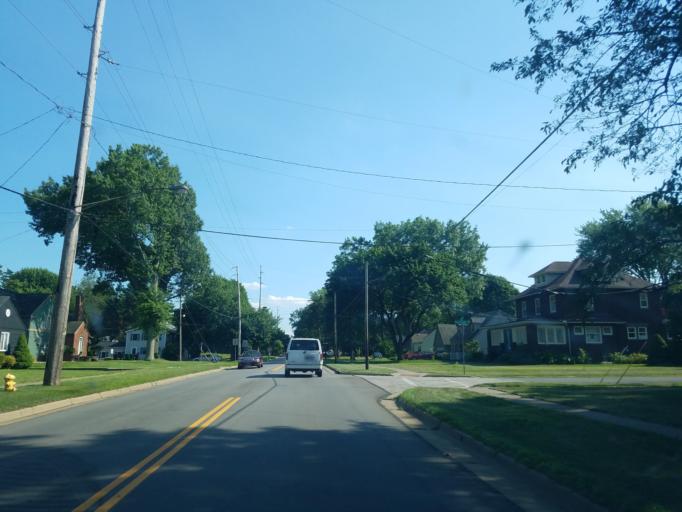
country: US
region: Ohio
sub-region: Summit County
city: Mogadore
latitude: 41.0421
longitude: -81.3931
